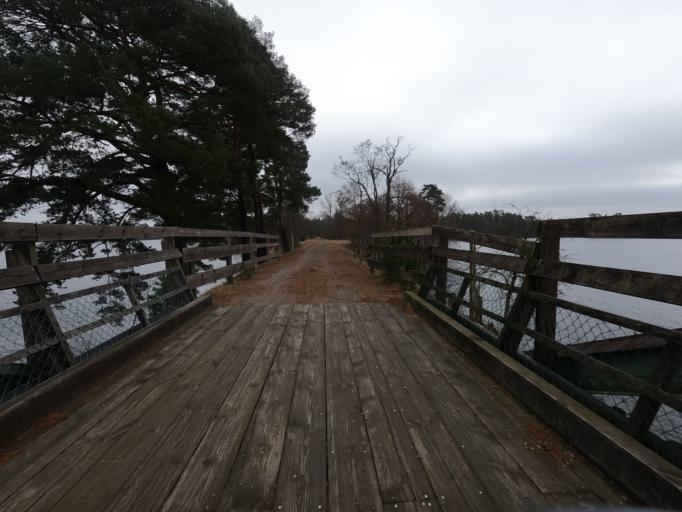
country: SE
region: Kronoberg
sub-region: Markaryds Kommun
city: Stromsnasbruk
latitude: 56.7875
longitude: 13.6464
